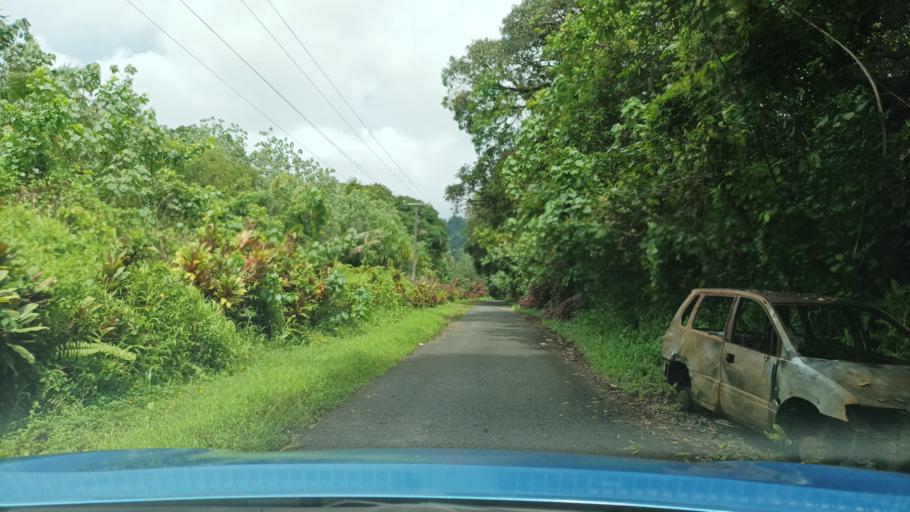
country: FM
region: Pohnpei
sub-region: Madolenihm Municipality
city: Madolenihm Municipality Government
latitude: 6.8877
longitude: 158.3154
